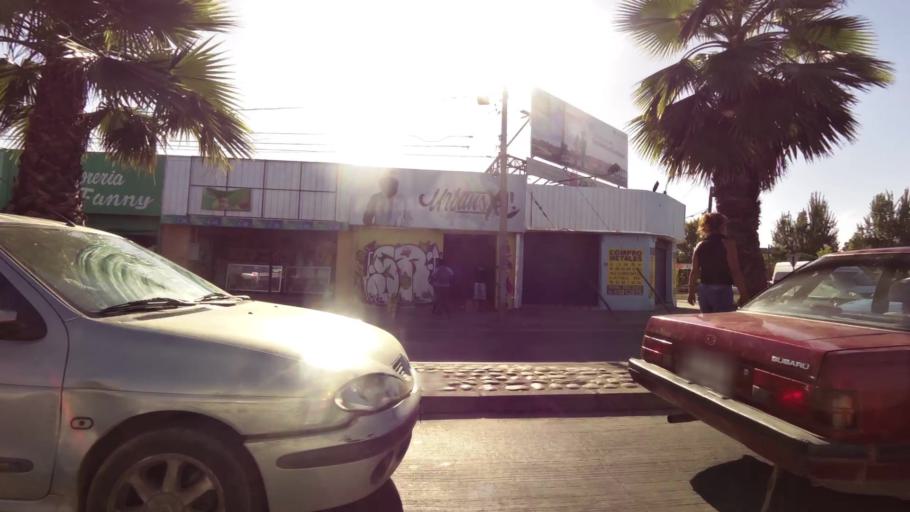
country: CL
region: Maule
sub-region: Provincia de Talca
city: Talca
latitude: -35.4236
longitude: -71.6498
